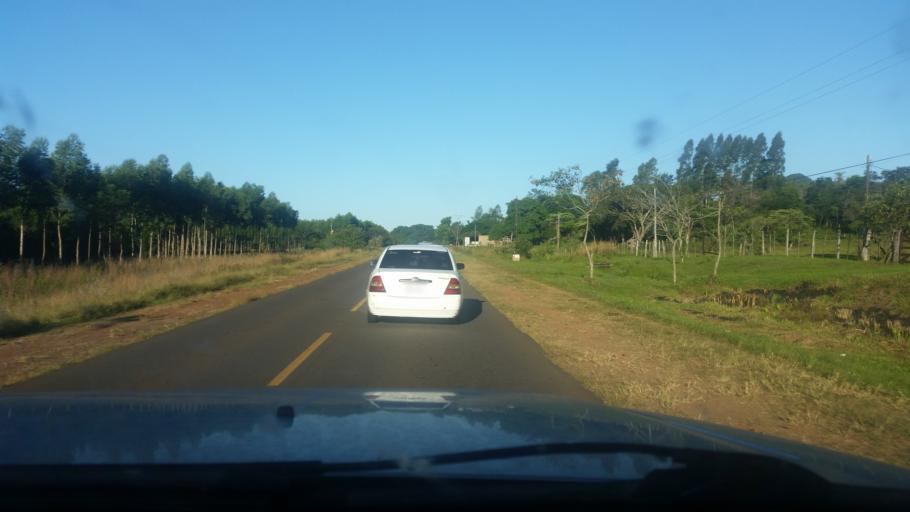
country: PY
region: Guaira
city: Independencia
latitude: -25.7247
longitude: -56.3084
